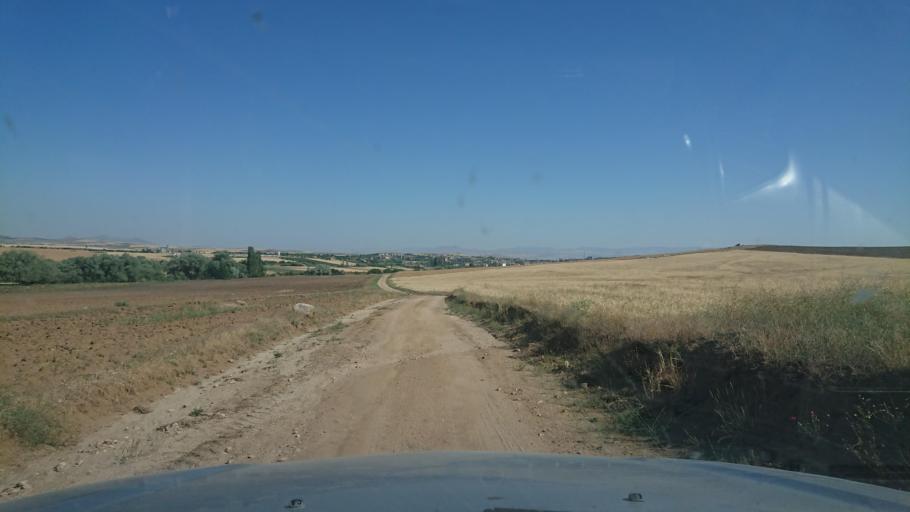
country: TR
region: Aksaray
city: Agacoren
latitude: 38.8499
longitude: 33.9159
